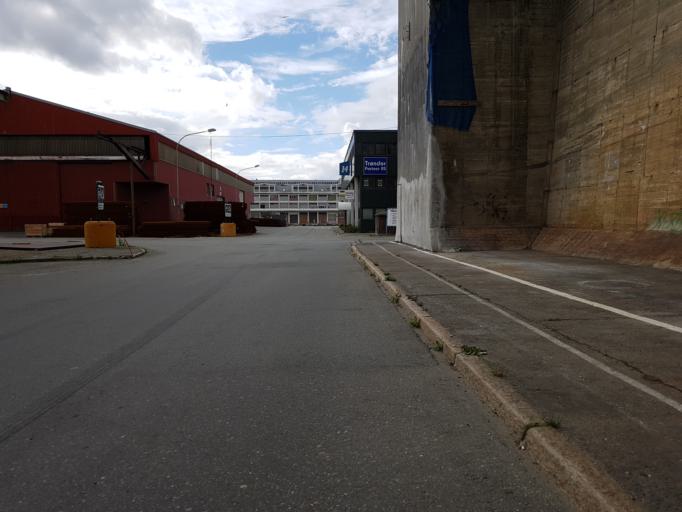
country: NO
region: Sor-Trondelag
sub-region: Trondheim
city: Trondheim
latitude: 63.4401
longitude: 10.4161
